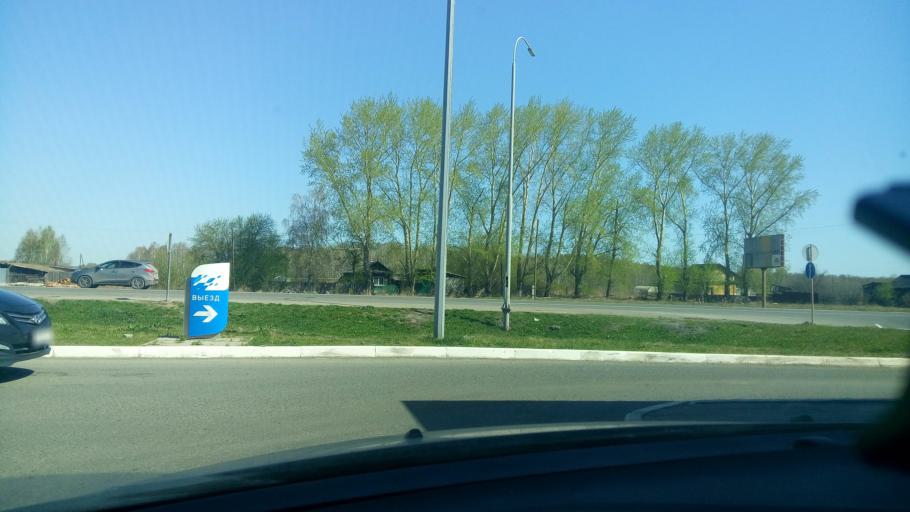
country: RU
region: Sverdlovsk
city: Bogdanovich
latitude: 56.7424
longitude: 62.0951
